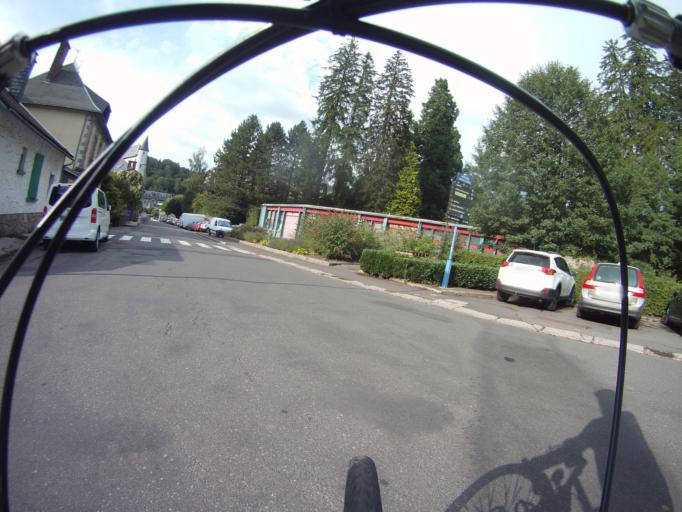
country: FR
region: Auvergne
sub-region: Departement du Puy-de-Dome
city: La Bourboule
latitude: 45.5862
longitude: 2.7387
